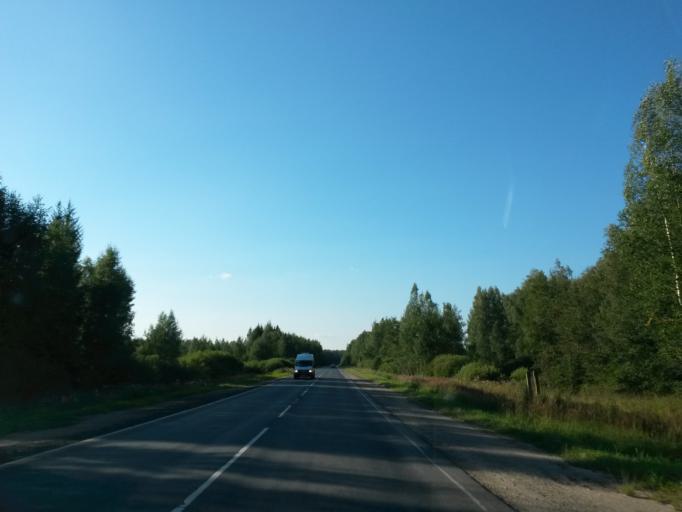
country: RU
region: Ivanovo
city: Pistsovo
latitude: 57.0954
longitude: 40.6599
